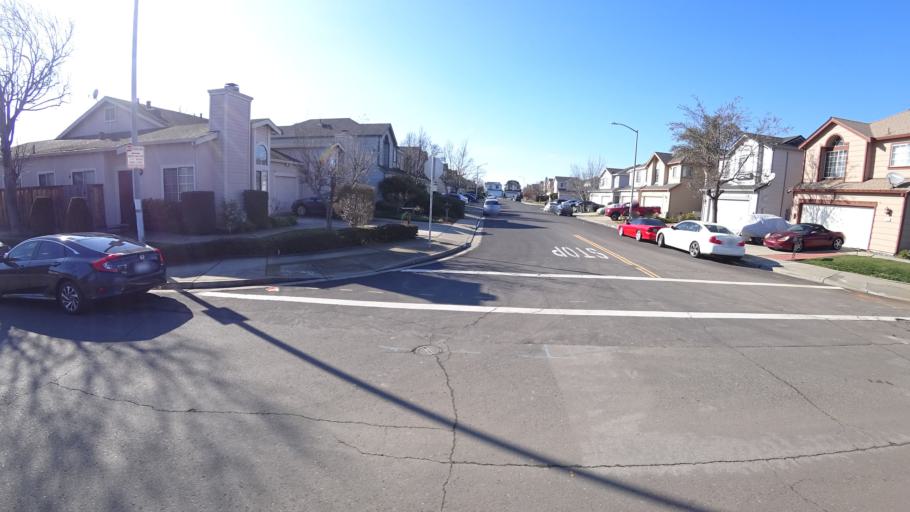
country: US
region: California
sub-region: Alameda County
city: Cherryland
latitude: 37.6437
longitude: -122.1154
